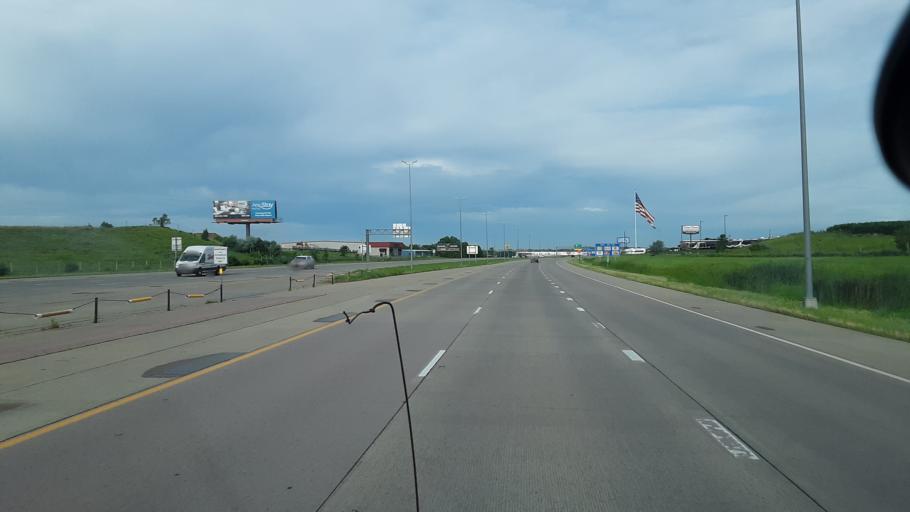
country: US
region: South Dakota
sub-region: Minnehaha County
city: Sioux Falls
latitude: 43.6061
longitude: -96.6993
